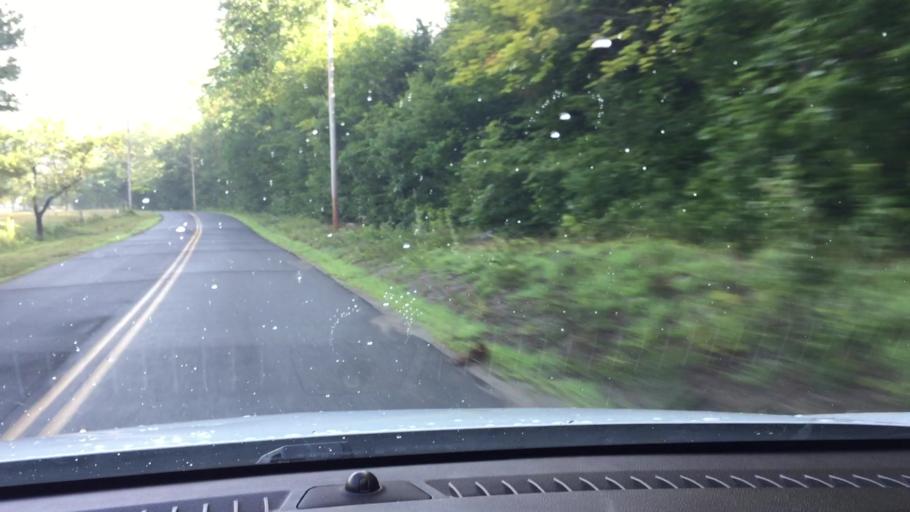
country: US
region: Massachusetts
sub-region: Berkshire County
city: Becket
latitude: 42.3934
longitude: -72.9774
